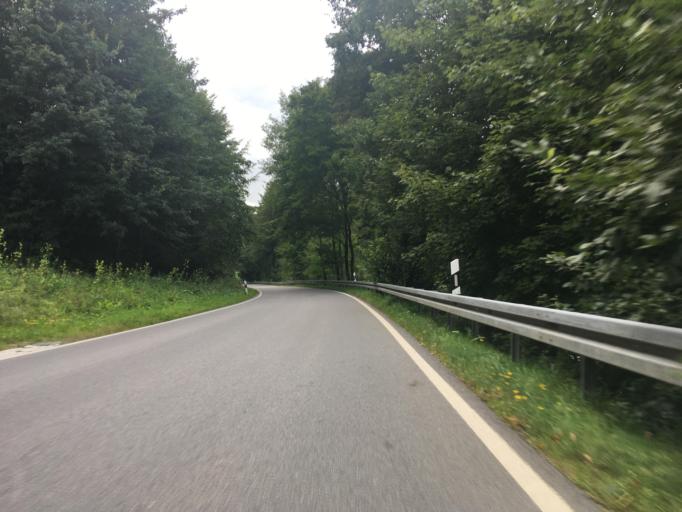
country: CZ
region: Ustecky
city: Mikulasovice
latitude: 50.9271
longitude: 14.3361
